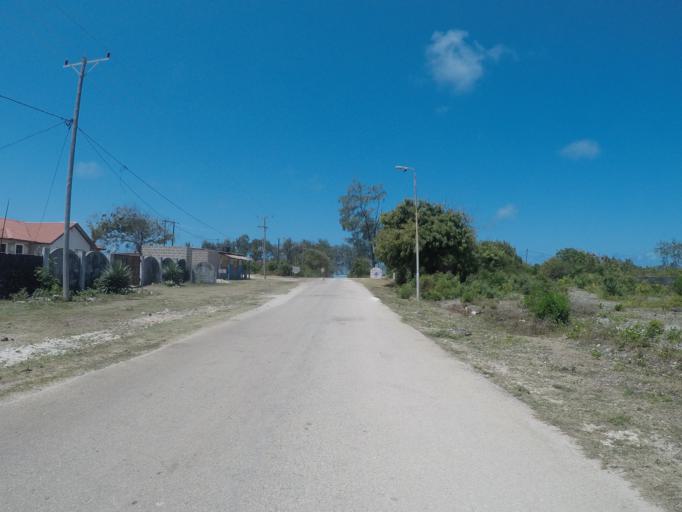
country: TZ
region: Zanzibar Central/South
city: Nganane
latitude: -6.4103
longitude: 39.5715
